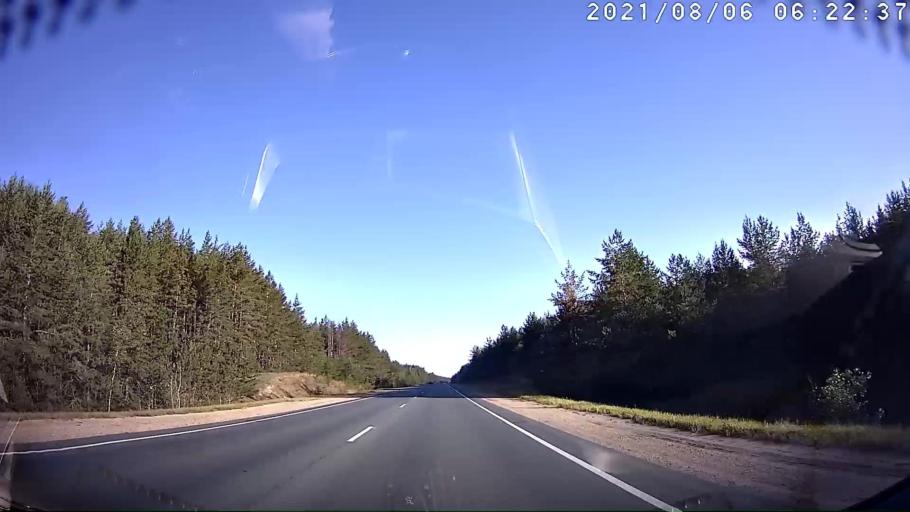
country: RU
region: Mariy-El
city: Krasnogorskiy
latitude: 56.0836
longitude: 48.3541
